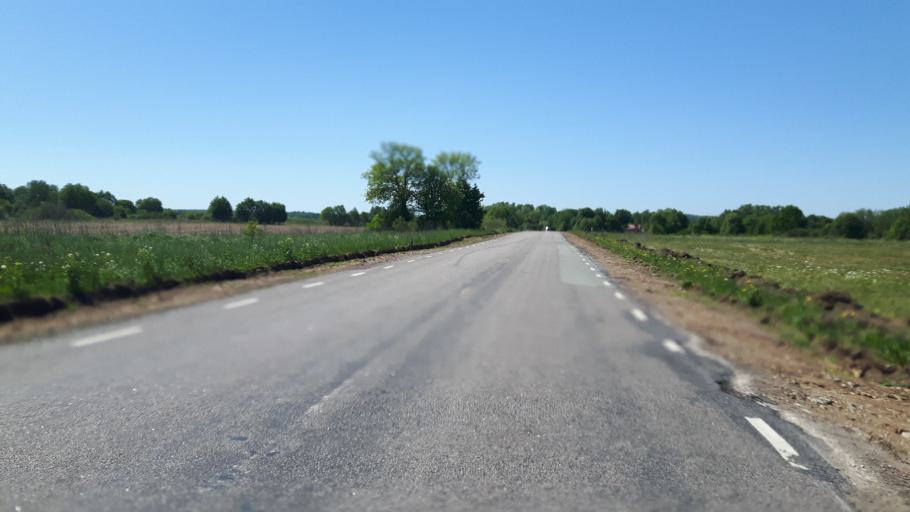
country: EE
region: Ida-Virumaa
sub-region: Narva-Joesuu linn
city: Narva-Joesuu
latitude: 59.3964
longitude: 27.9284
